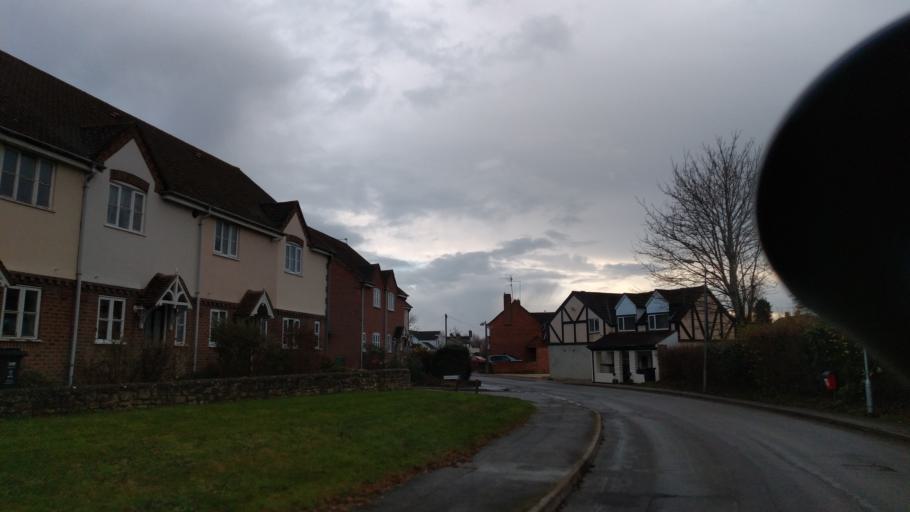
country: GB
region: England
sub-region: Borough of Swindon
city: Highworth
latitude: 51.5916
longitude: -1.7247
